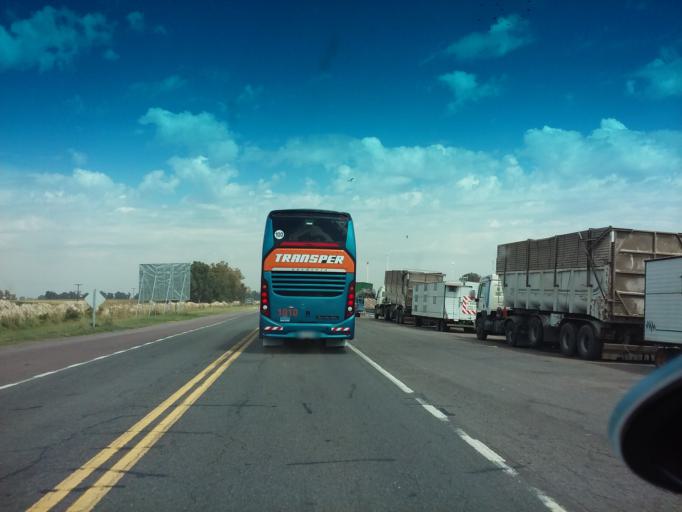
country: AR
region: Buenos Aires
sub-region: Partido de Carlos Casares
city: Carlos Casares
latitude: -35.6570
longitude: -61.3987
